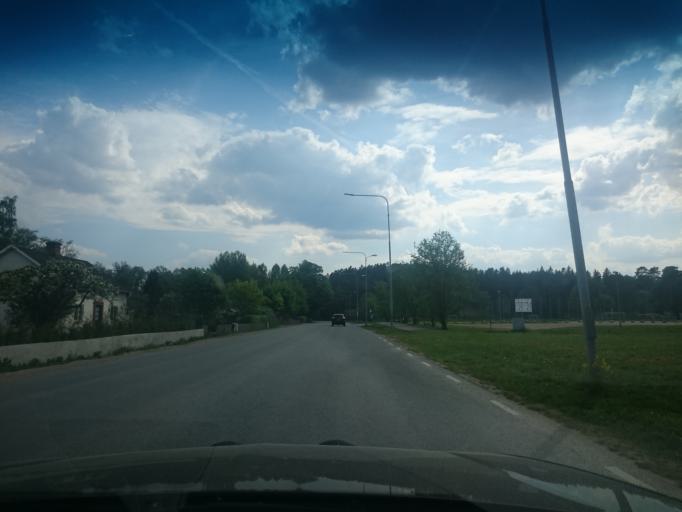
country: SE
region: Joenkoeping
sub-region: Vetlanda Kommun
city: Vetlanda
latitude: 57.4406
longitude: 15.0703
